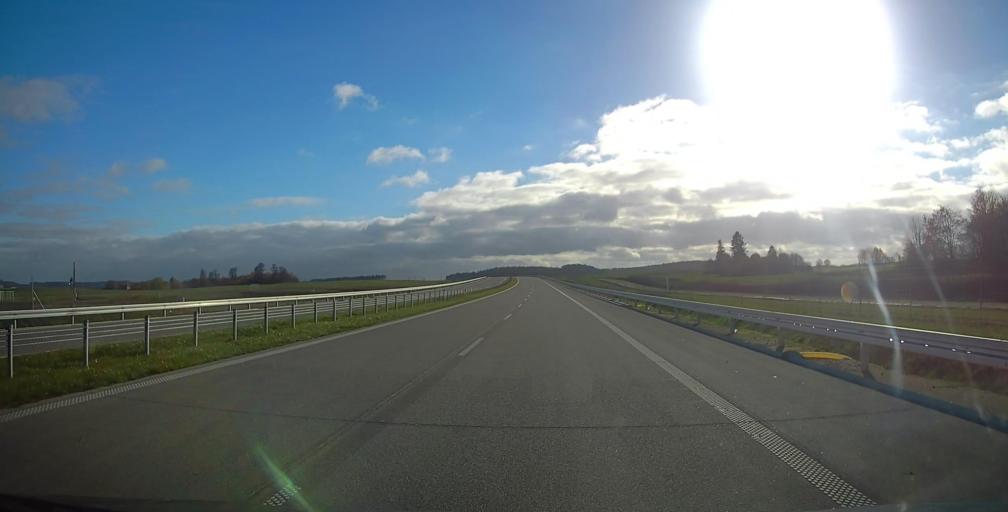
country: PL
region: Warmian-Masurian Voivodeship
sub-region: Powiat elcki
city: Elk
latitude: 53.7168
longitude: 22.2802
